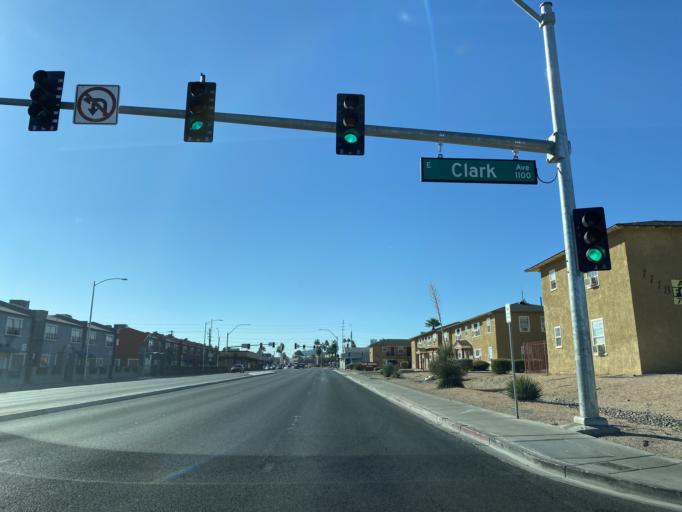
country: US
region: Nevada
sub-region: Clark County
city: Las Vegas
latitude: 36.1612
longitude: -115.1357
